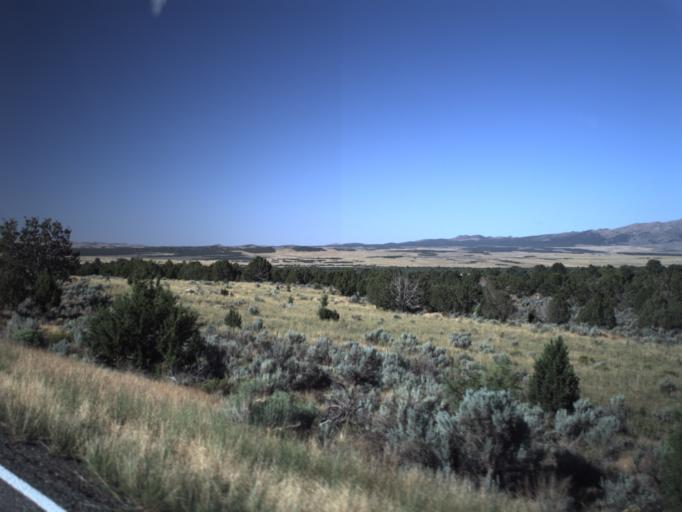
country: US
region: Utah
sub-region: Utah County
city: Genola
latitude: 39.9350
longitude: -112.1494
